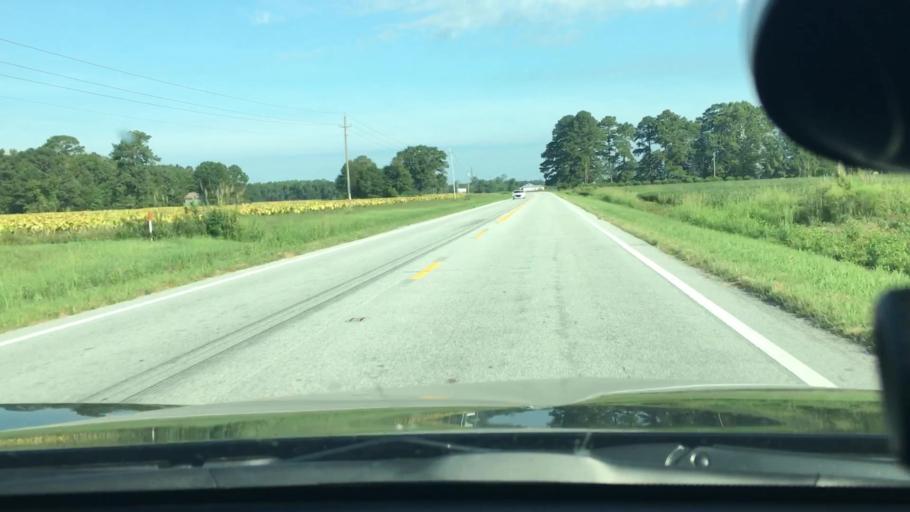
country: US
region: North Carolina
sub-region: Pitt County
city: Summerfield
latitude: 35.6664
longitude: -77.4778
